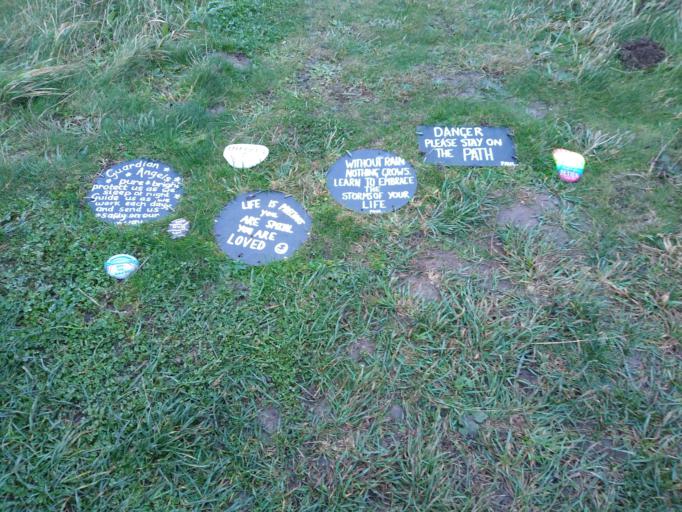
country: GB
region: England
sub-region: Redcar and Cleveland
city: Saltburn-by-the-Sea
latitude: 54.5879
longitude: -0.9440
